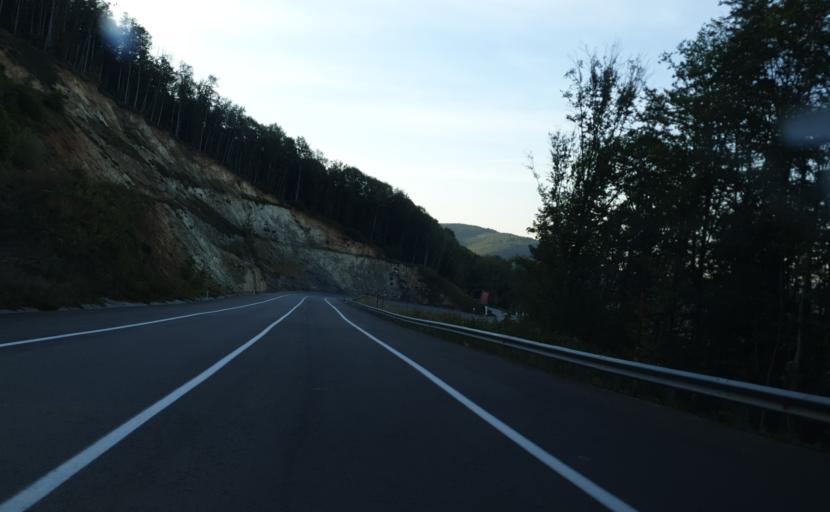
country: TR
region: Kirklareli
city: Sergen
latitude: 41.8133
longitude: 27.7459
